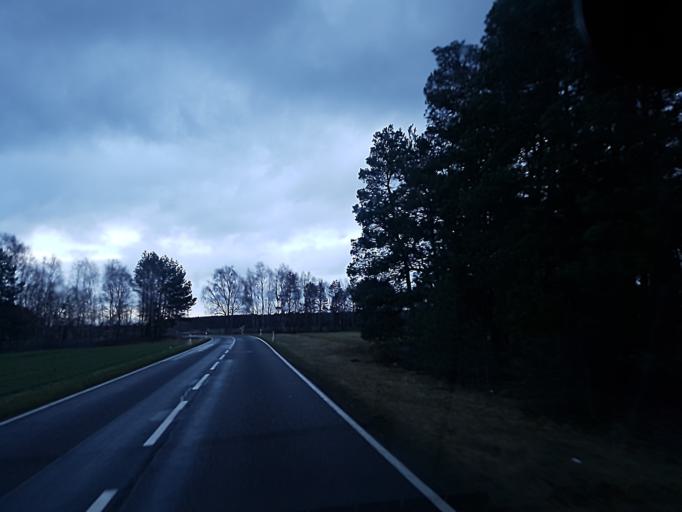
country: DE
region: Brandenburg
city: Finsterwalde
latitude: 51.5574
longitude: 13.6734
